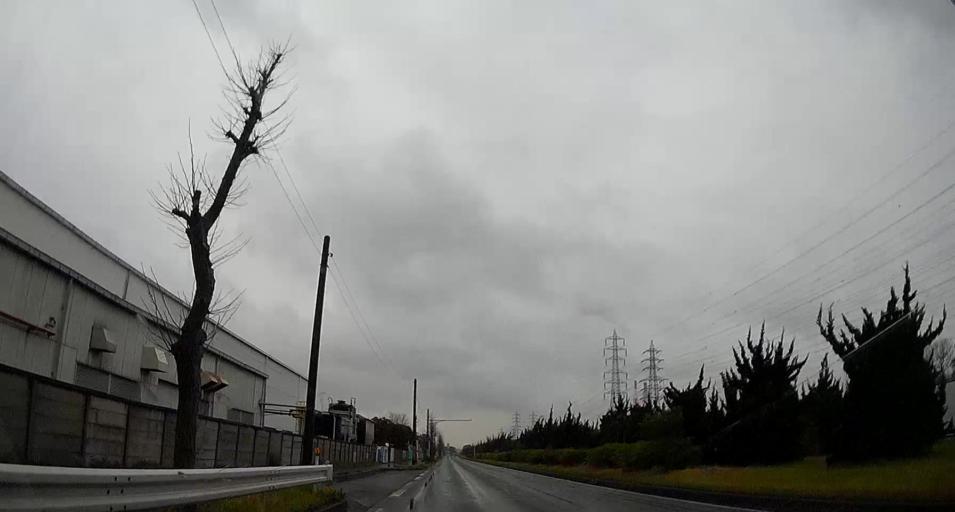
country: JP
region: Chiba
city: Ichihara
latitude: 35.4937
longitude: 140.0452
